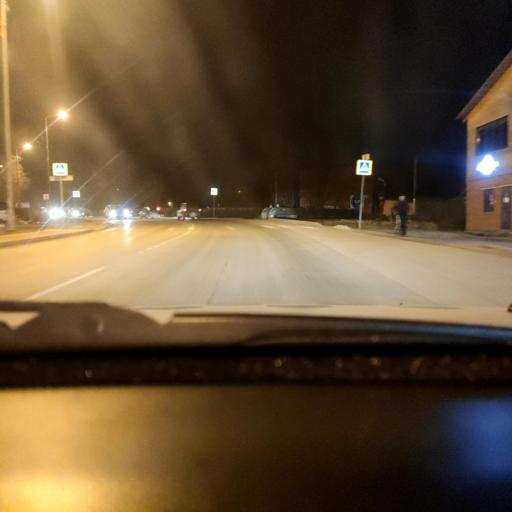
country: RU
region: Perm
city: Kondratovo
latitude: 57.9645
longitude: 56.1539
